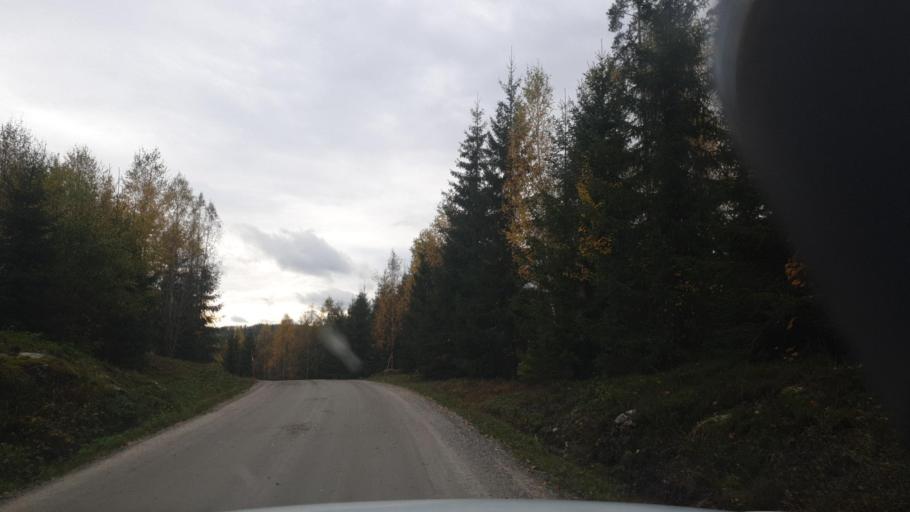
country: SE
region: Vaermland
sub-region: Arvika Kommun
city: Arvika
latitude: 59.8229
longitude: 12.7428
